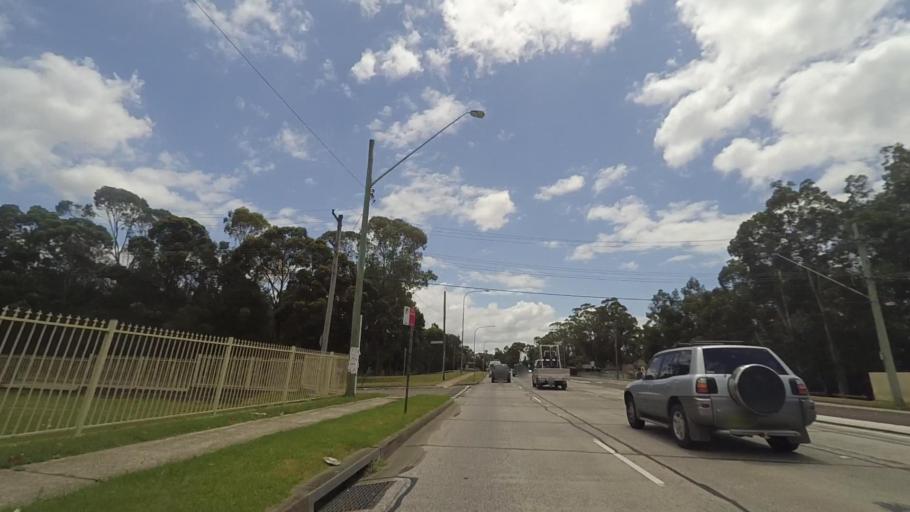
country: AU
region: New South Wales
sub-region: Fairfield
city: Fairfield Heights
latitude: -33.8755
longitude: 150.9254
